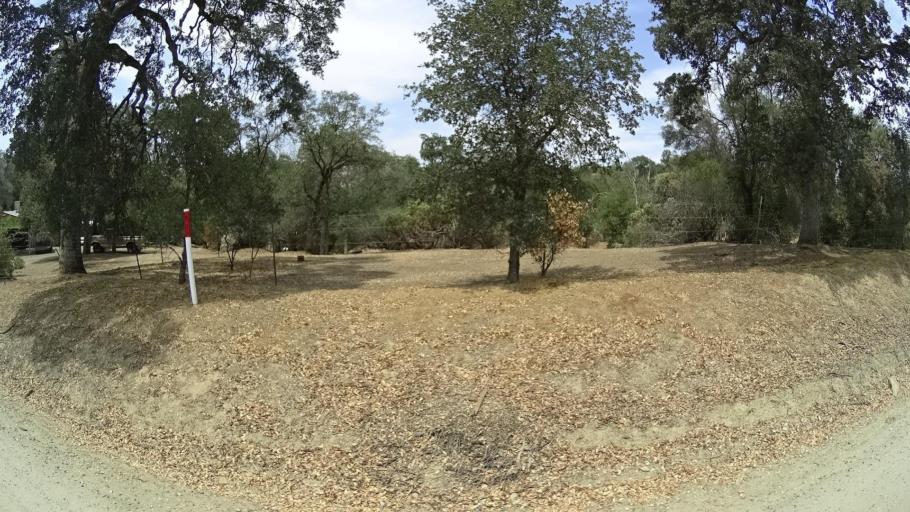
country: US
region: California
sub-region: Madera County
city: Ahwahnee
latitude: 37.4109
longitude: -119.8214
